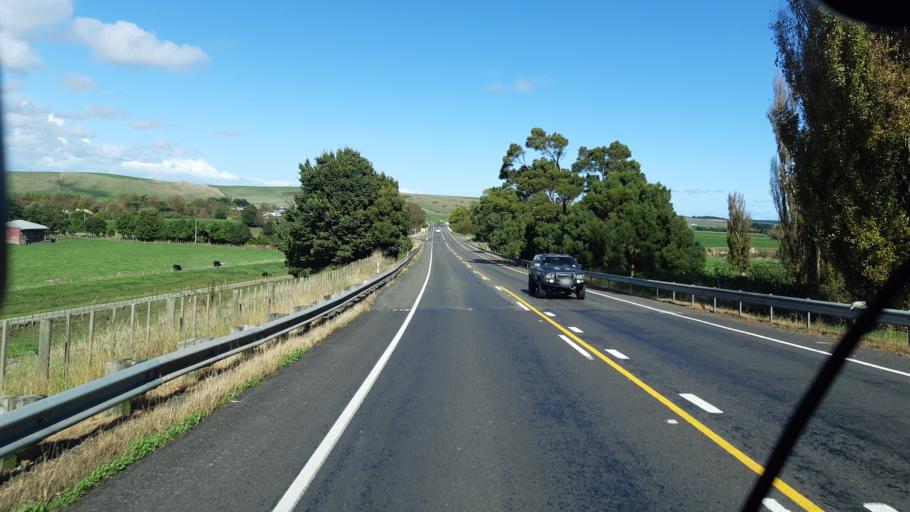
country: NZ
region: Manawatu-Wanganui
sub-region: Wanganui District
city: Wanganui
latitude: -40.0017
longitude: 175.1668
